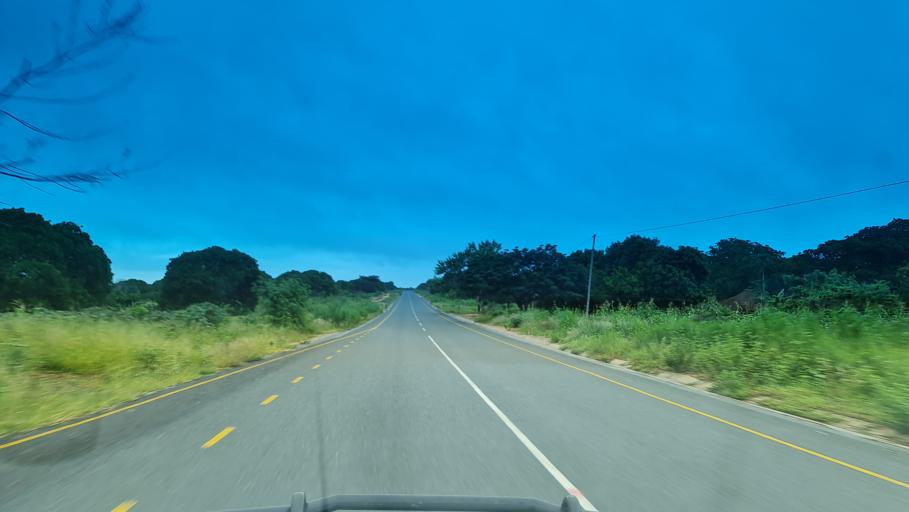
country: MZ
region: Nampula
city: Nampula
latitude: -15.6183
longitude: 39.3335
